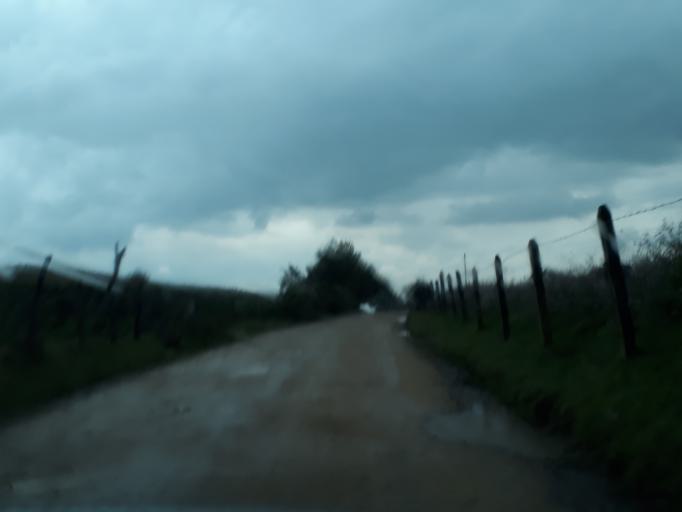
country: CO
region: Cundinamarca
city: Villapinzon
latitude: 5.3026
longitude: -73.5921
